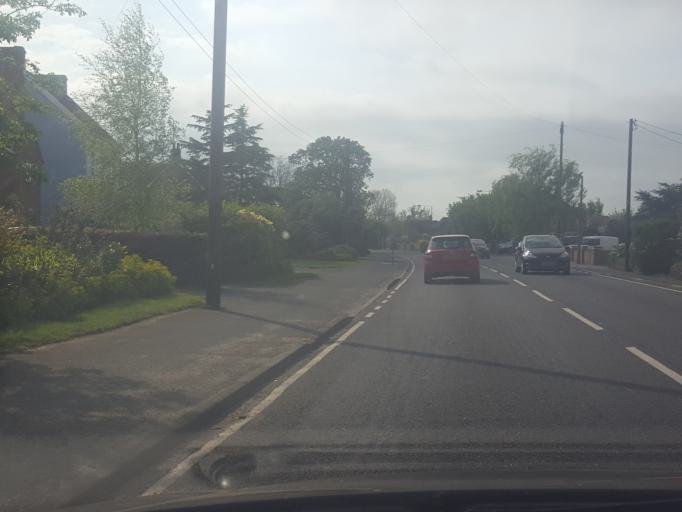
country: GB
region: England
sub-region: Essex
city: Frinton-on-Sea
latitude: 51.8413
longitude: 1.2362
